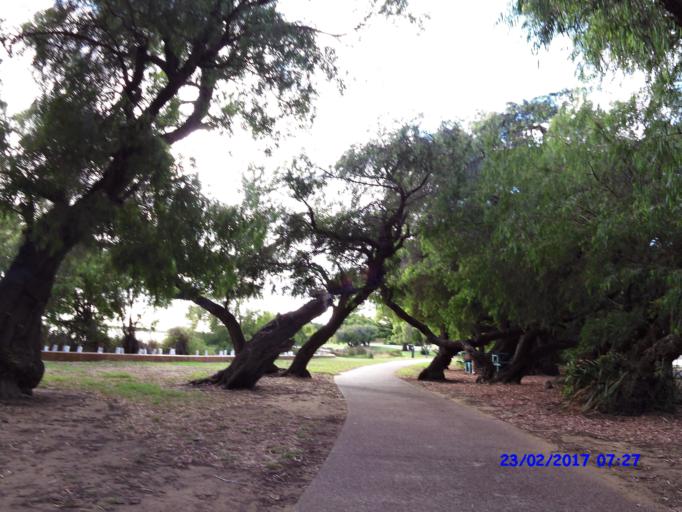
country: AU
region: Western Australia
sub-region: Augusta-Margaret River Shire
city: Augusta
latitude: -34.3241
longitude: 115.1655
